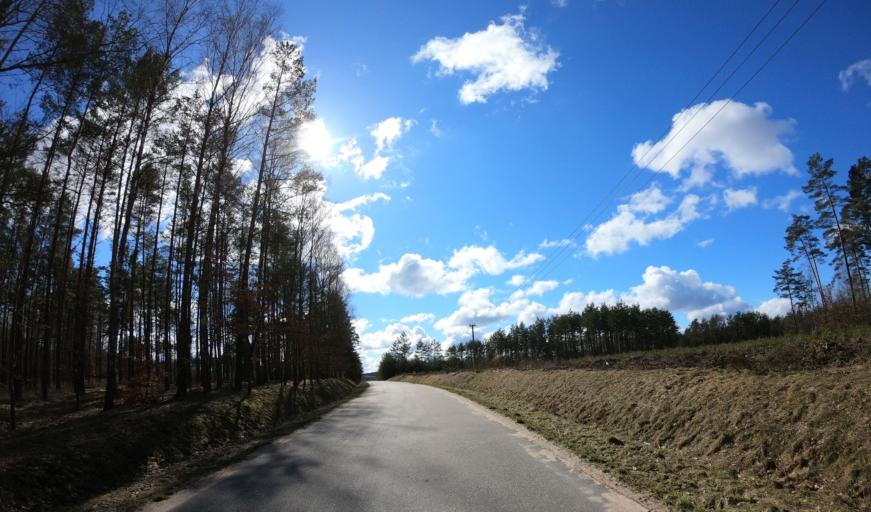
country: PL
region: West Pomeranian Voivodeship
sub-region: Powiat drawski
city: Zlocieniec
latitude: 53.4847
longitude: 15.9809
